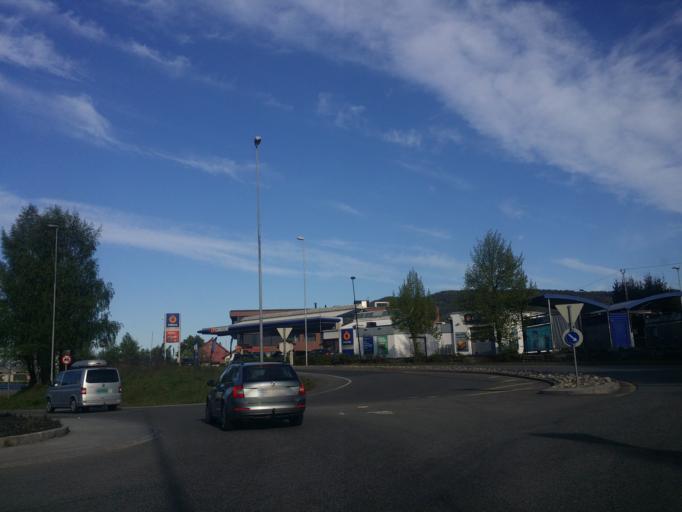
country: NO
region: Buskerud
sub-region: Nedre Eiker
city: Mjondalen
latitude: 59.7526
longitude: 10.0027
